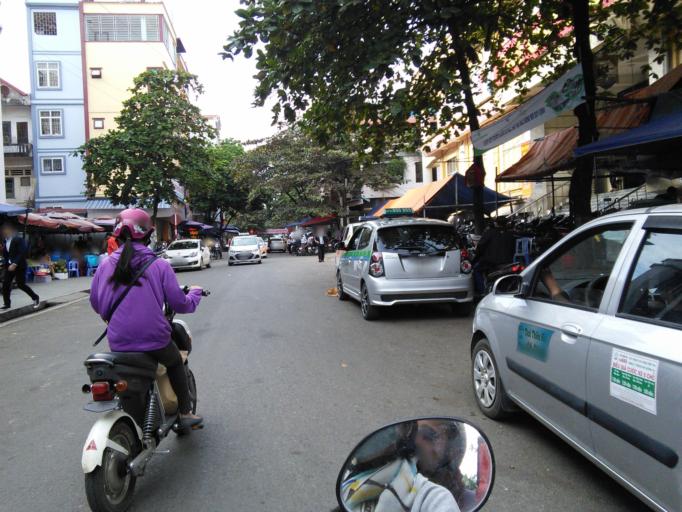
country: VN
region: Lao Cai
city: Lao Cai
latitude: 22.5010
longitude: 103.9681
